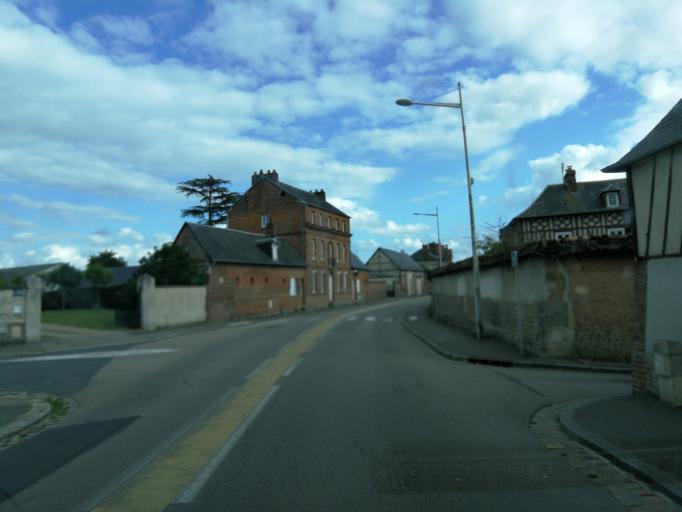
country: FR
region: Haute-Normandie
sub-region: Departement de l'Eure
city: Le Neubourg
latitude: 49.1451
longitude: 0.9024
